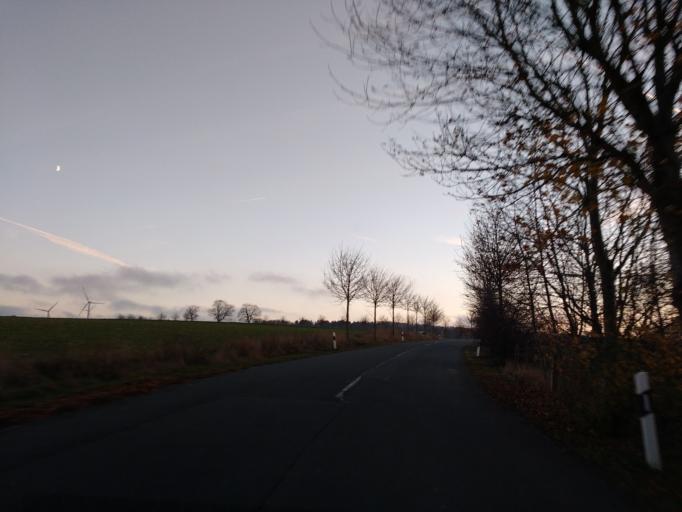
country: DE
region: North Rhine-Westphalia
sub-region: Regierungsbezirk Detmold
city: Paderborn
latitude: 51.6936
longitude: 8.7991
